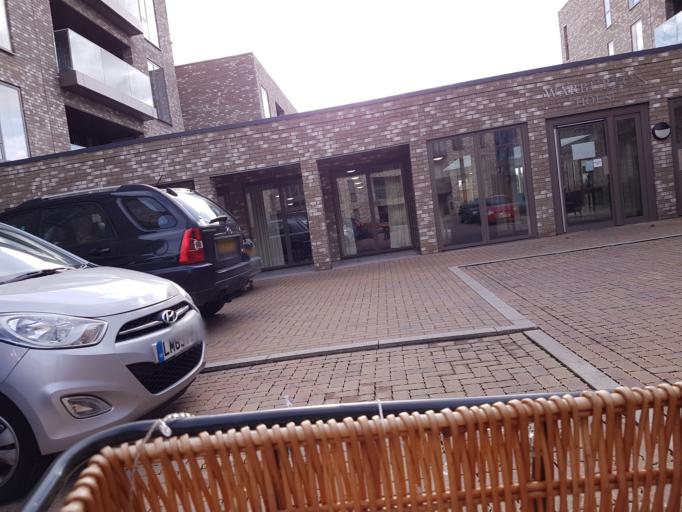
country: GB
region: England
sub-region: Cambridgeshire
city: Cambridge
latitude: 52.1721
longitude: 0.1423
